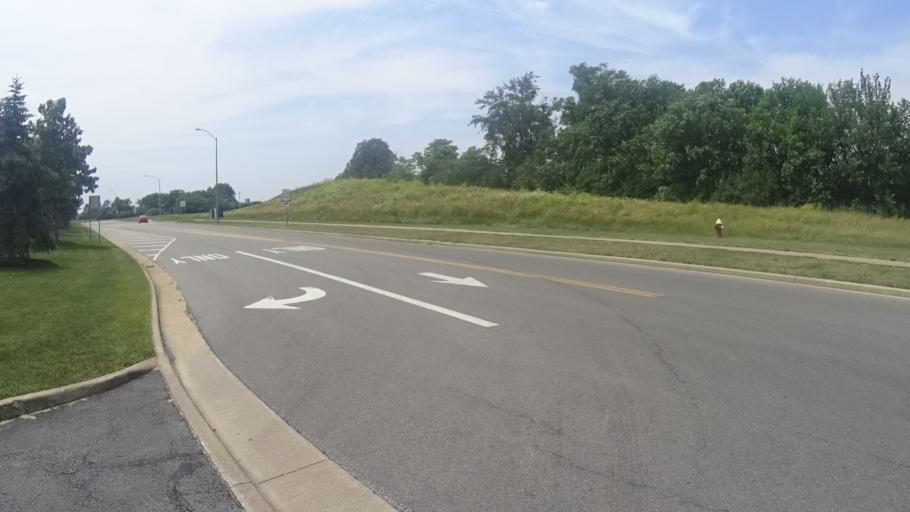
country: US
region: Ohio
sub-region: Erie County
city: Huron
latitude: 41.3869
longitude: -82.6421
